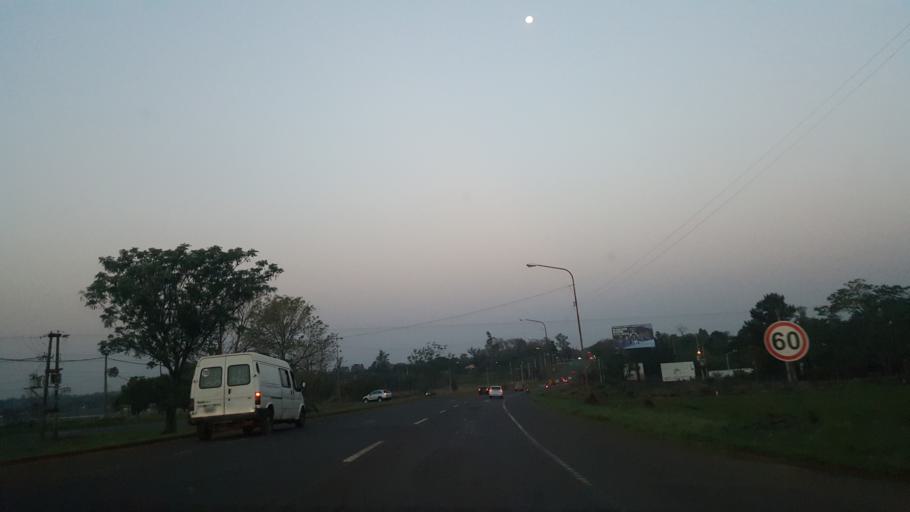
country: AR
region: Misiones
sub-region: Departamento de Capital
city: Posadas
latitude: -27.3984
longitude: -55.9598
